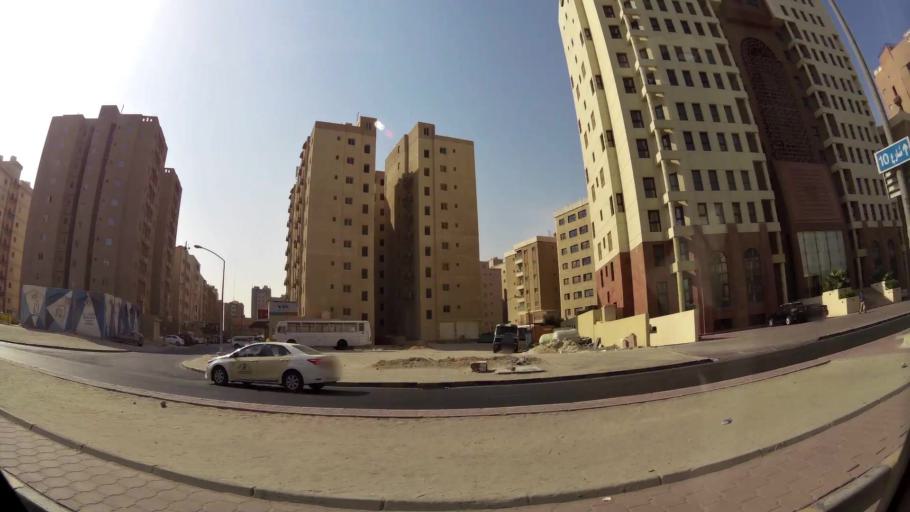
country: KW
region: Al Ahmadi
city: Al Fintas
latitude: 29.1584
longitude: 48.1164
